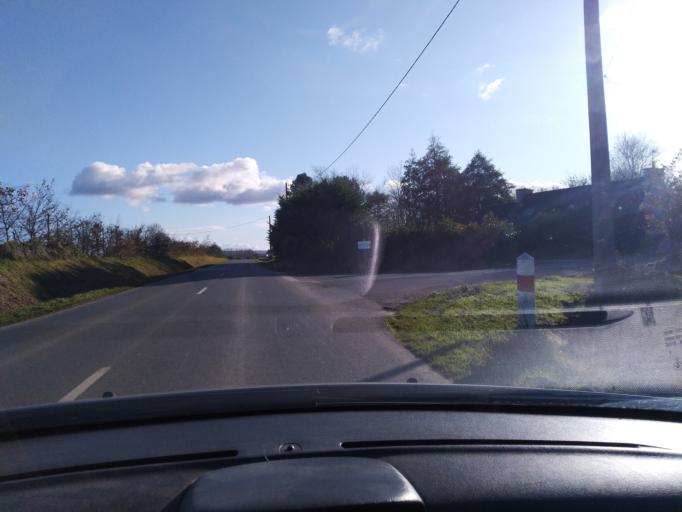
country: FR
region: Brittany
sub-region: Departement des Cotes-d'Armor
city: Plestin-les-Greves
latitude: 48.6357
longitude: -3.6178
